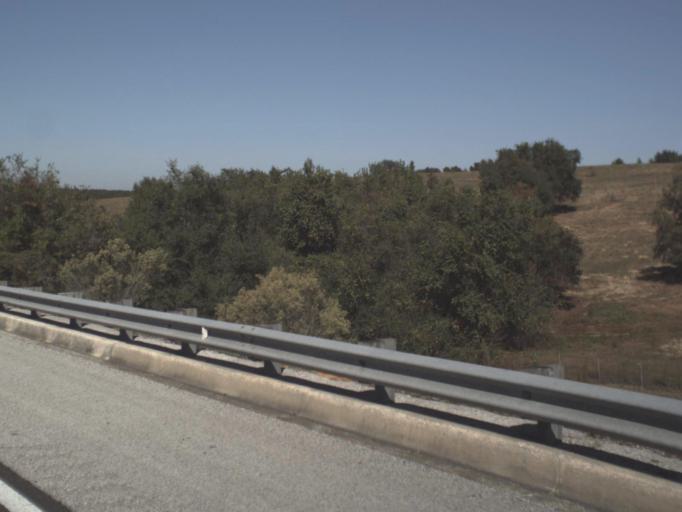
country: US
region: Florida
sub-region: Lake County
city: Minneola
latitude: 28.6160
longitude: -81.7393
